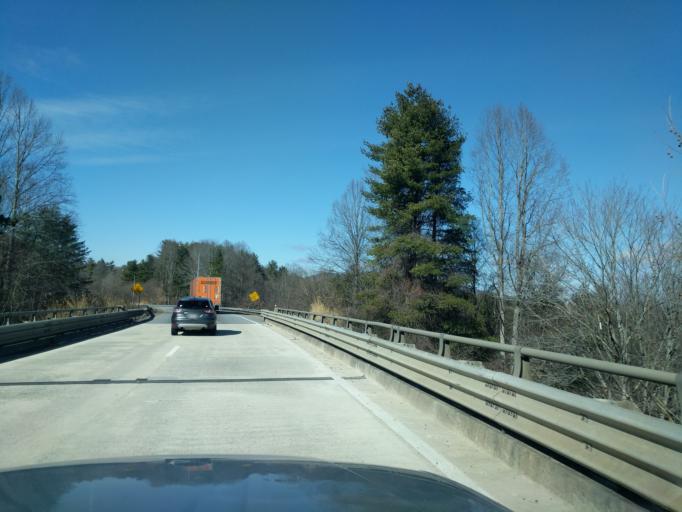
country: US
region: North Carolina
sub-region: Buncombe County
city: Bent Creek
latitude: 35.5545
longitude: -82.6116
